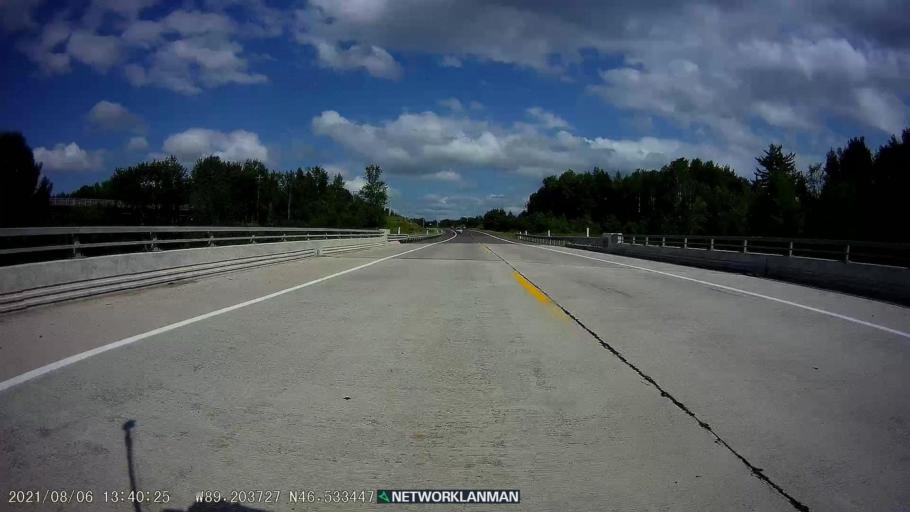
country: US
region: Michigan
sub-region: Ontonagon County
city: Ontonagon
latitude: 46.5333
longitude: -89.2053
